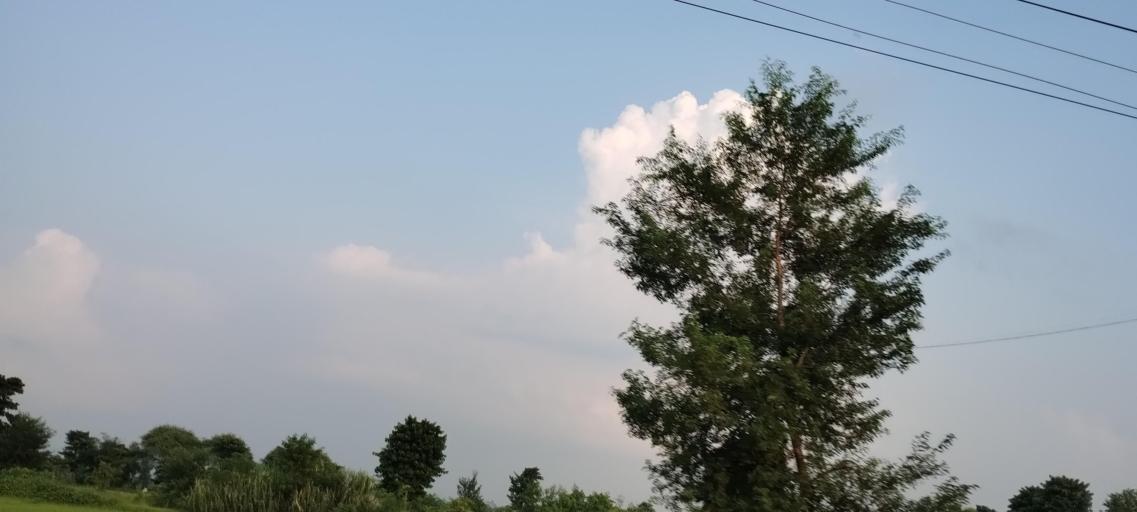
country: NP
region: Far Western
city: Tikapur
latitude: 28.4735
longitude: 81.2786
